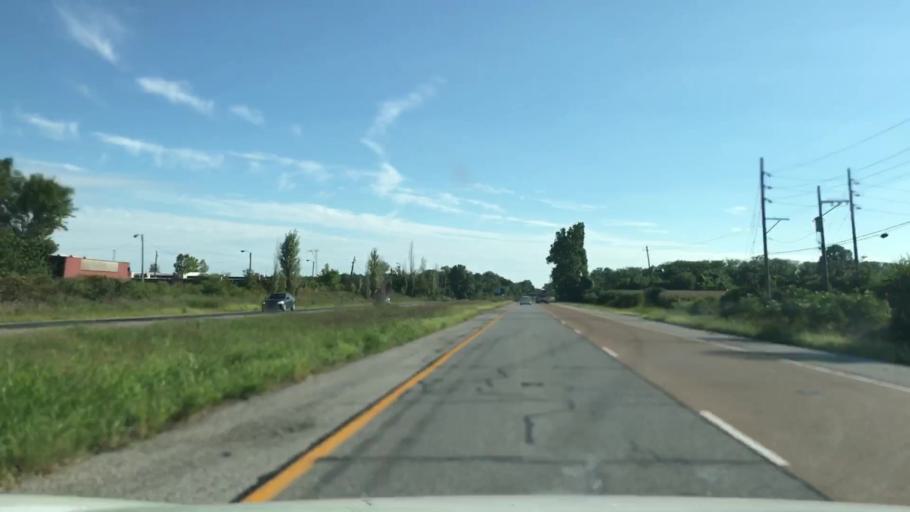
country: US
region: Illinois
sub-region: Madison County
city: Hartford
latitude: 38.7996
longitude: -90.1009
